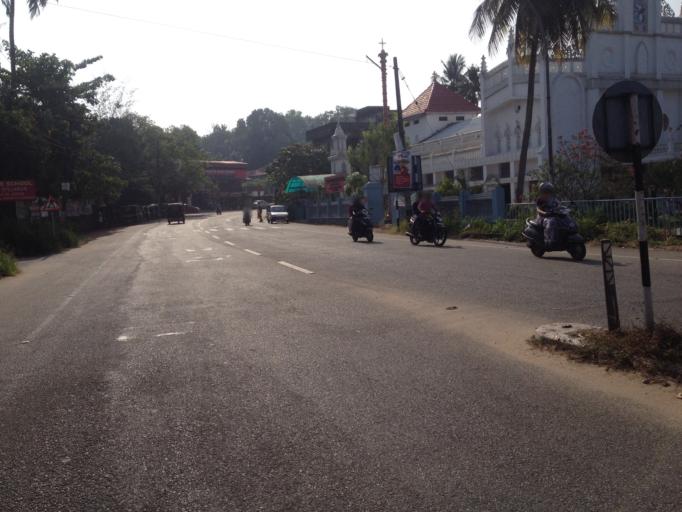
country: IN
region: Kerala
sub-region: Pattanamtitta
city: Adur
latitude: 9.1617
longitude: 76.7232
